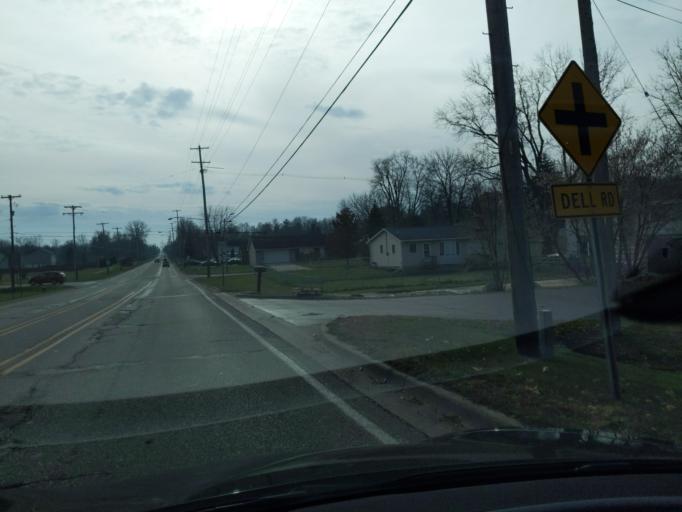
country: US
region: Michigan
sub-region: Ingham County
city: Holt
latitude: 42.6627
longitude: -84.5235
